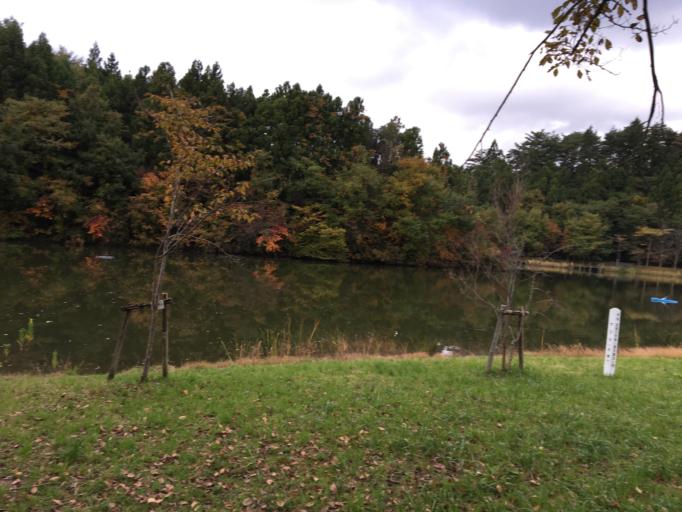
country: JP
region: Miyagi
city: Tomiya
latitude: 38.3496
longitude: 140.8413
